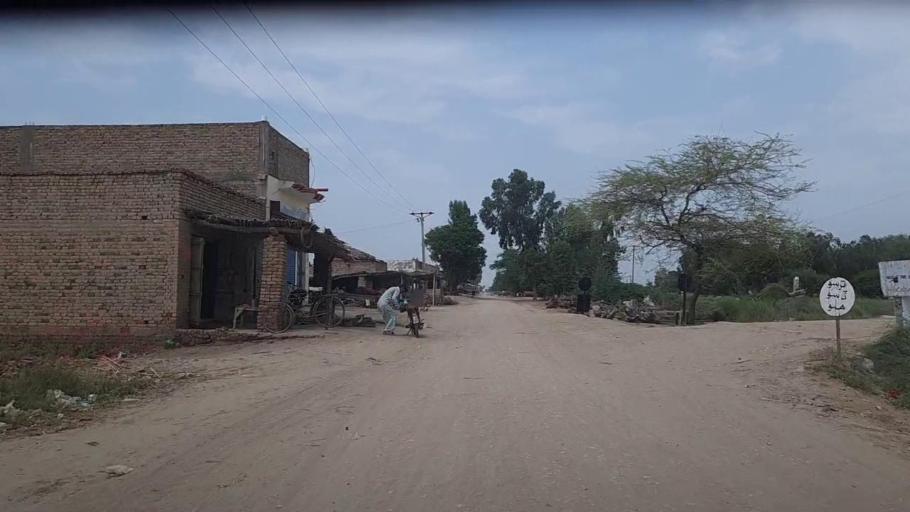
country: PK
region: Sindh
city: Bhiria
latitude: 26.8956
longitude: 68.2864
